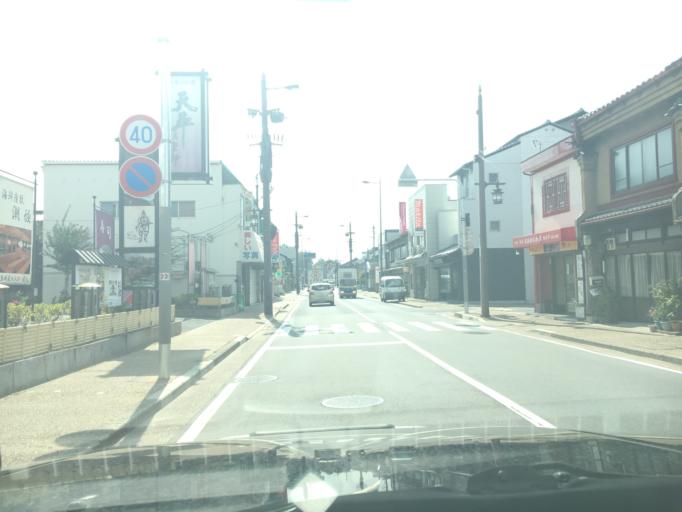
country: JP
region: Nara
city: Nara-shi
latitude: 34.6909
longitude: 135.8347
